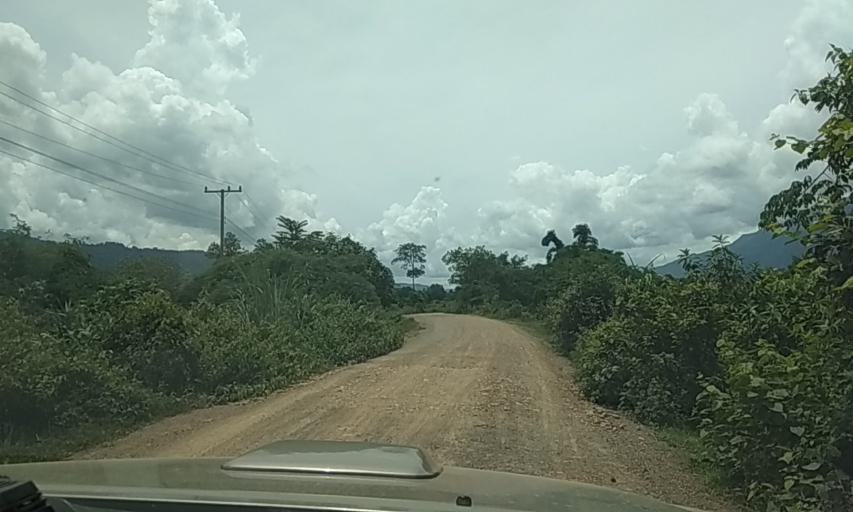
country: LA
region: Bolikhamxai
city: Ban Nahin
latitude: 18.1436
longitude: 104.7550
